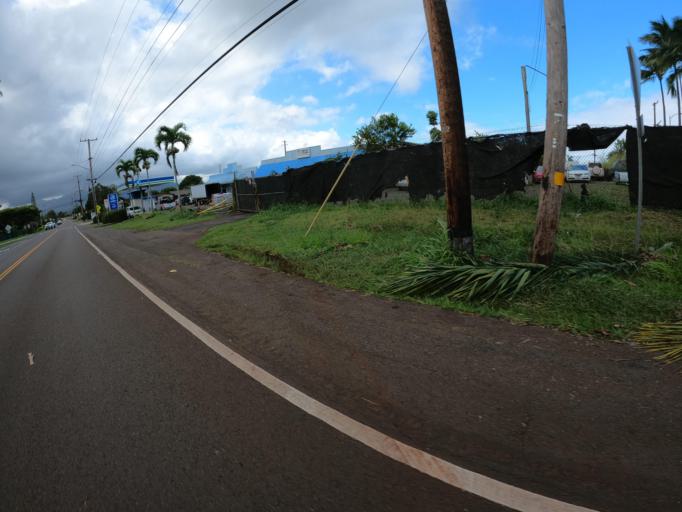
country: US
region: Hawaii
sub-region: Honolulu County
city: Whitmore Village
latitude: 21.5111
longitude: -158.0198
